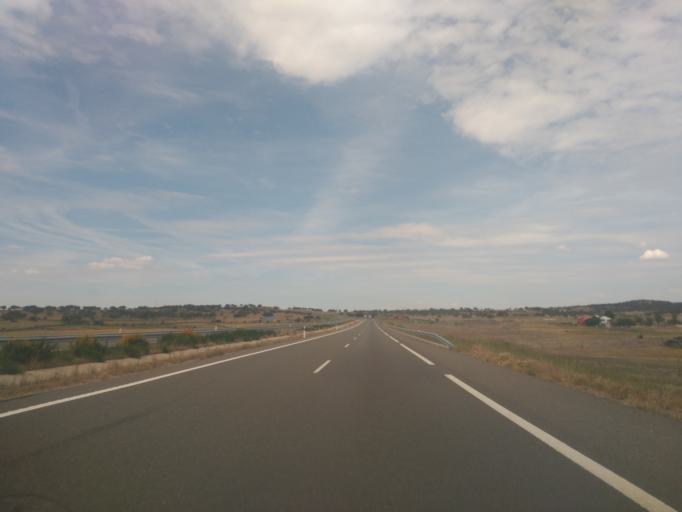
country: ES
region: Castille and Leon
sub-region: Provincia de Salamanca
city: Pizarral
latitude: 40.6090
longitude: -5.6426
